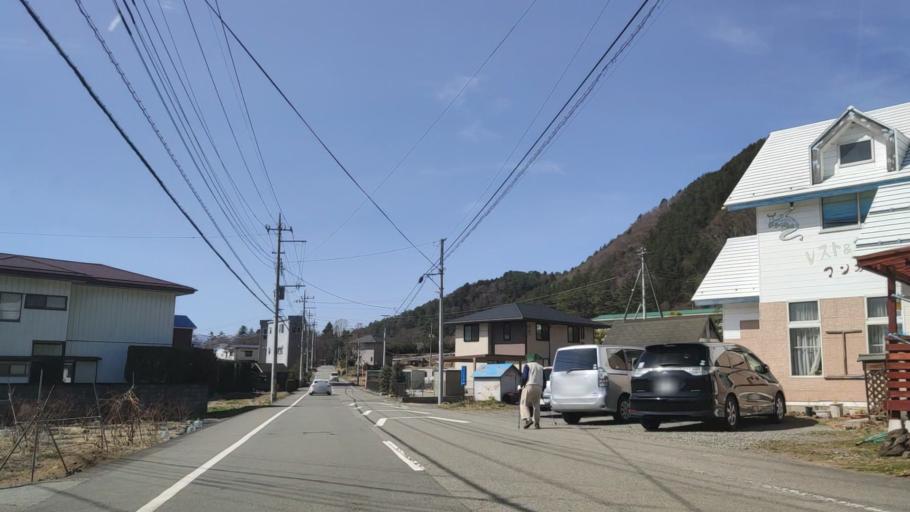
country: JP
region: Yamanashi
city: Fujikawaguchiko
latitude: 35.5283
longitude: 138.7640
